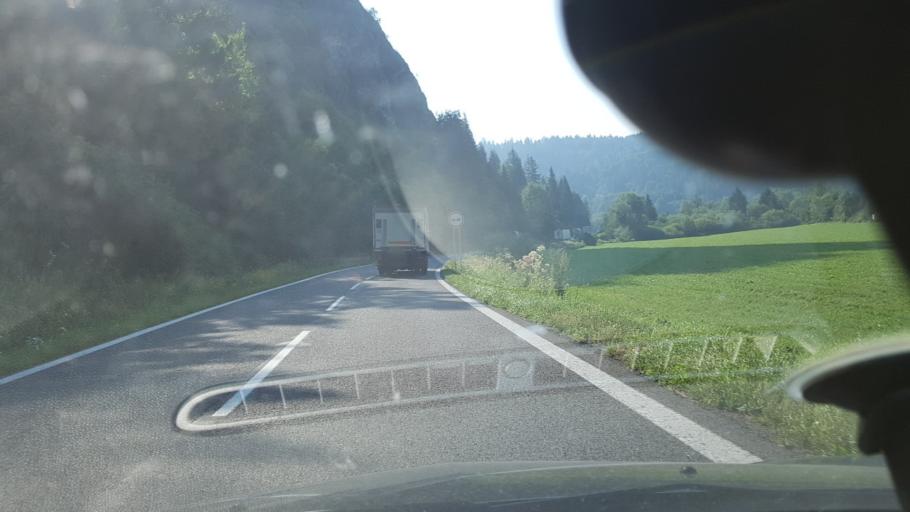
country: SK
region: Zilinsky
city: Tvrdosin
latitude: 49.2965
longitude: 19.4884
